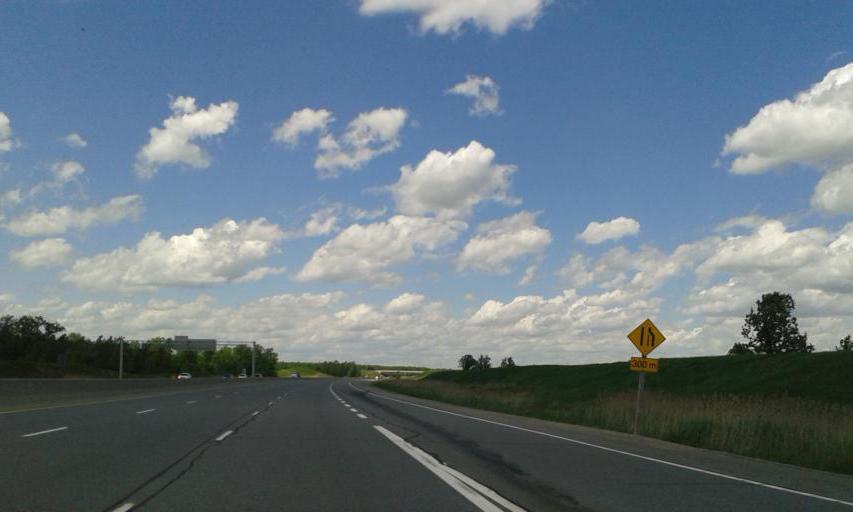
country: CA
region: Ontario
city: Burlington
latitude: 43.3904
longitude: -79.8338
